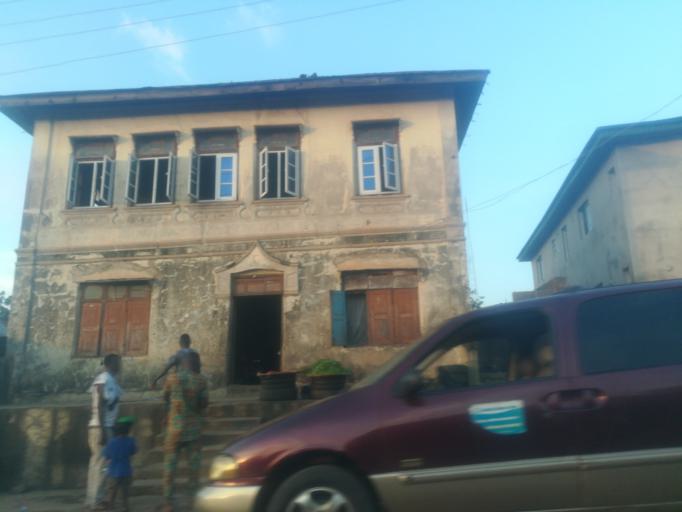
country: NG
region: Ogun
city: Abeokuta
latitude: 7.1492
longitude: 3.3329
